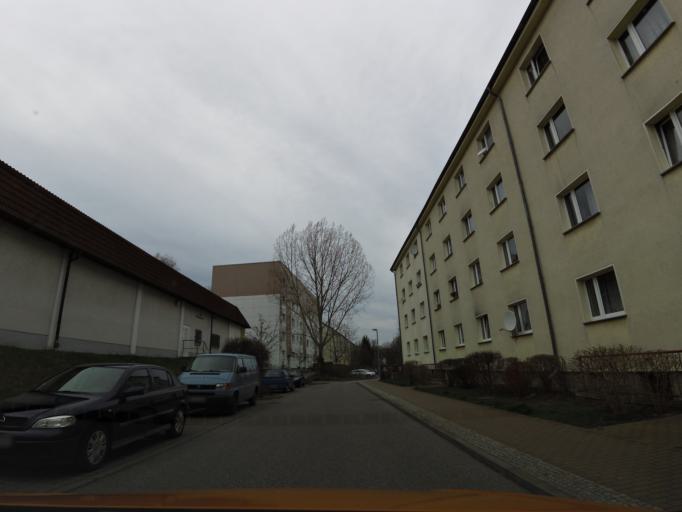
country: DE
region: Brandenburg
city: Belzig
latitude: 52.1390
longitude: 12.6051
